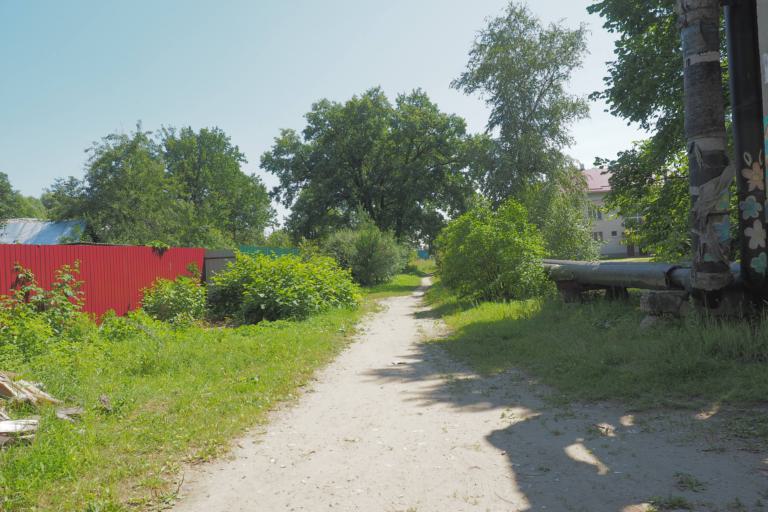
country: RU
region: Moskovskaya
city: Malyshevo
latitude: 55.5015
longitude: 38.3656
